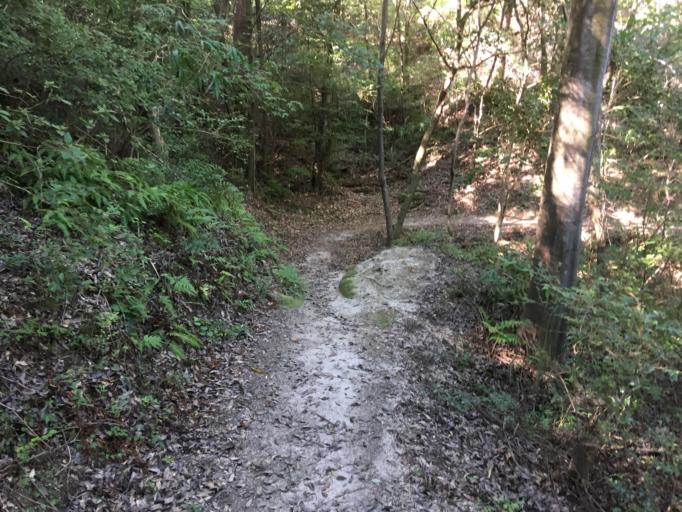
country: JP
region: Osaka
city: Neyagawa
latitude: 34.7481
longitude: 135.6827
